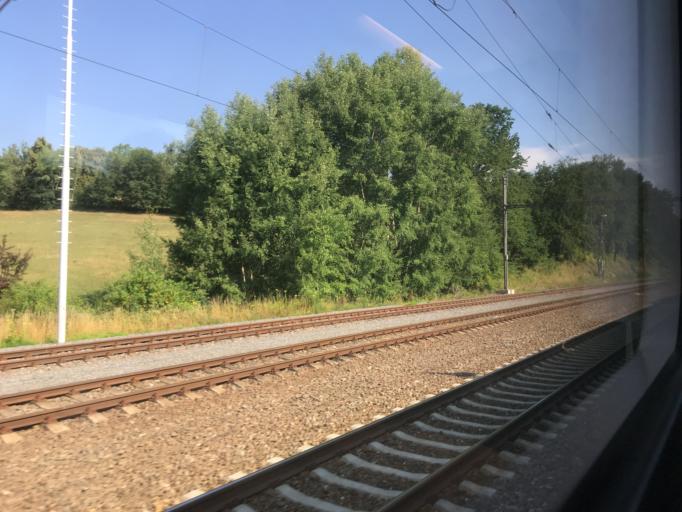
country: CZ
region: Central Bohemia
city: Votice
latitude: 49.6399
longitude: 14.6207
